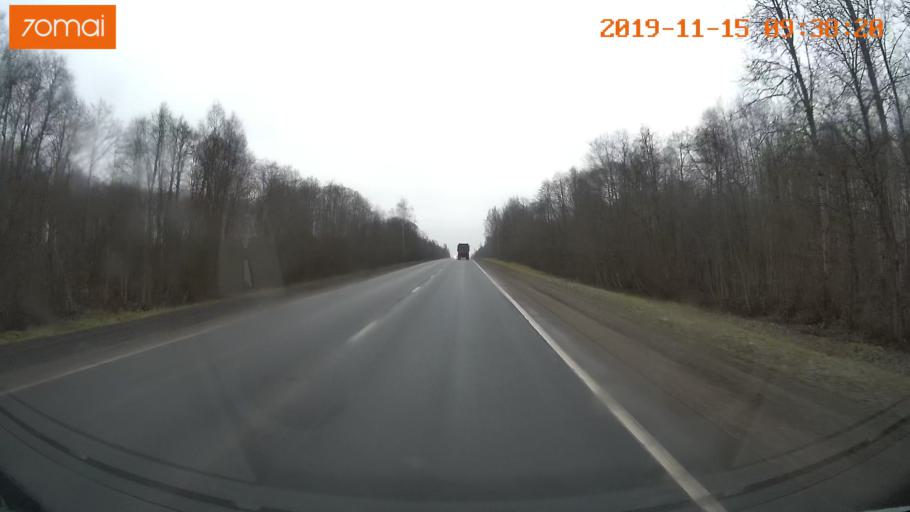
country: RU
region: Vologda
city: Sheksna
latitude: 59.2328
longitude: 38.4536
